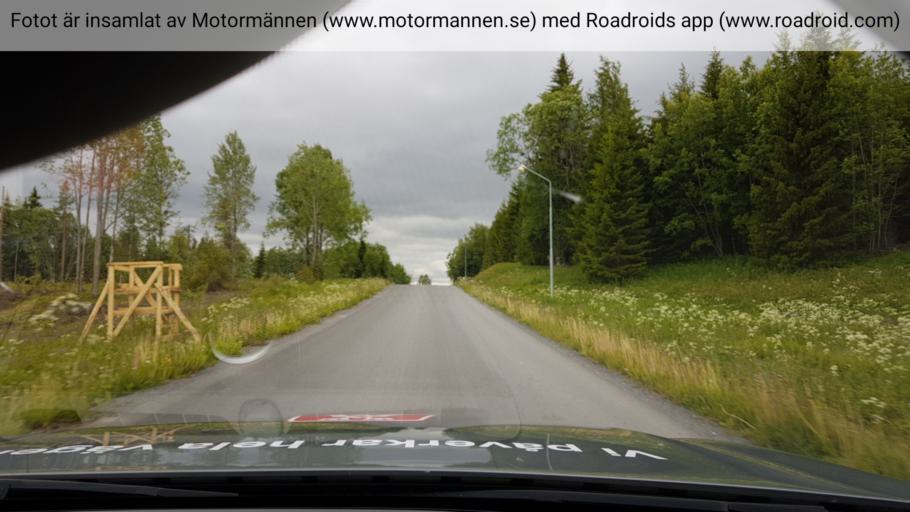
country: SE
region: Jaemtland
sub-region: OEstersunds Kommun
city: Lit
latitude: 63.5700
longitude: 14.9587
